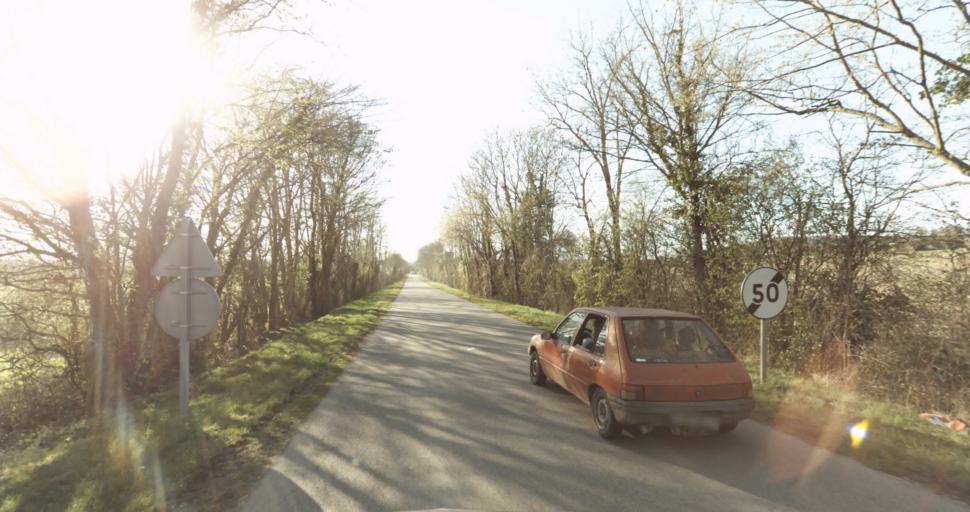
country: FR
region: Lower Normandy
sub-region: Departement du Calvados
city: Livarot
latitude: 48.9643
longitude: 0.0650
